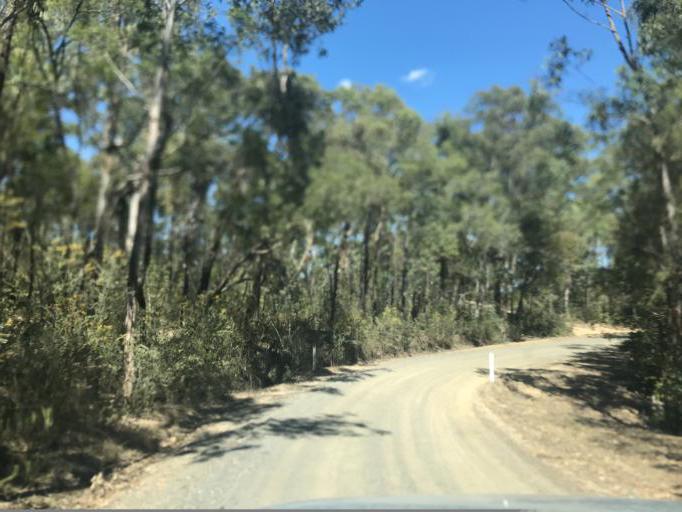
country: AU
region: New South Wales
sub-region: Wyong Shire
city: Little Jilliby
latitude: -33.1510
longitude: 151.0808
